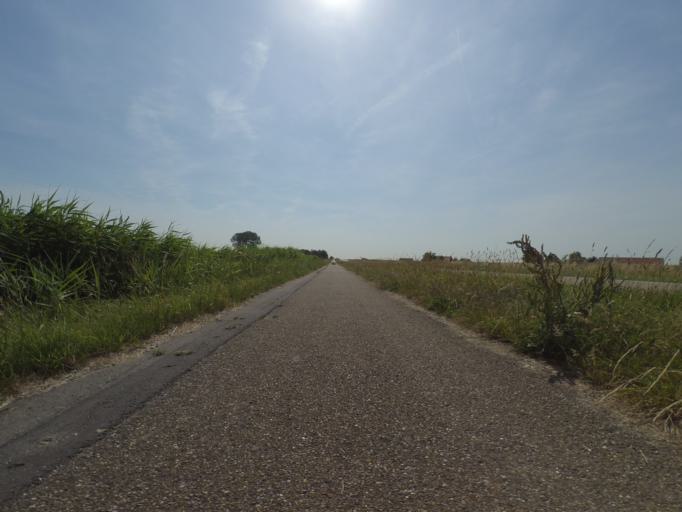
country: NL
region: Zeeland
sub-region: Schouwen-Duiveland
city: Bruinisse
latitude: 51.6306
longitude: 4.1327
